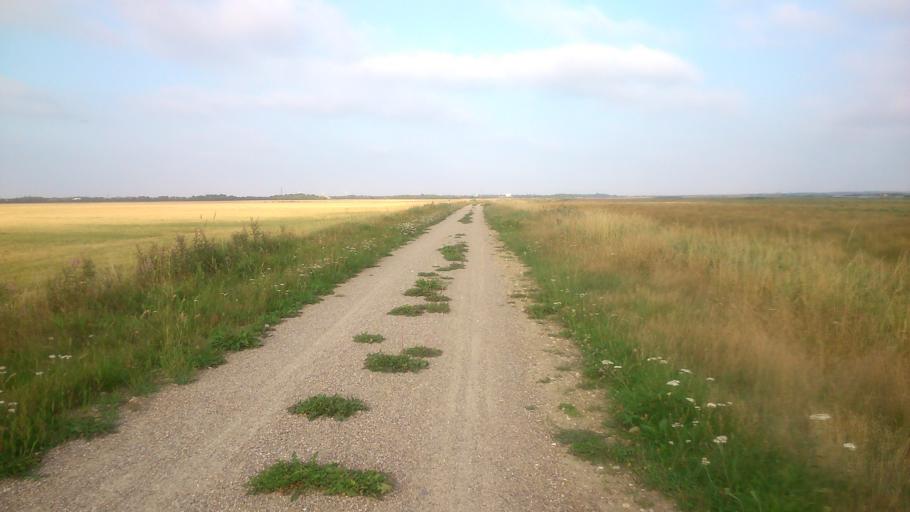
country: DK
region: Central Jutland
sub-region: Ringkobing-Skjern Kommune
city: Skjern
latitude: 55.9273
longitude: 8.4430
